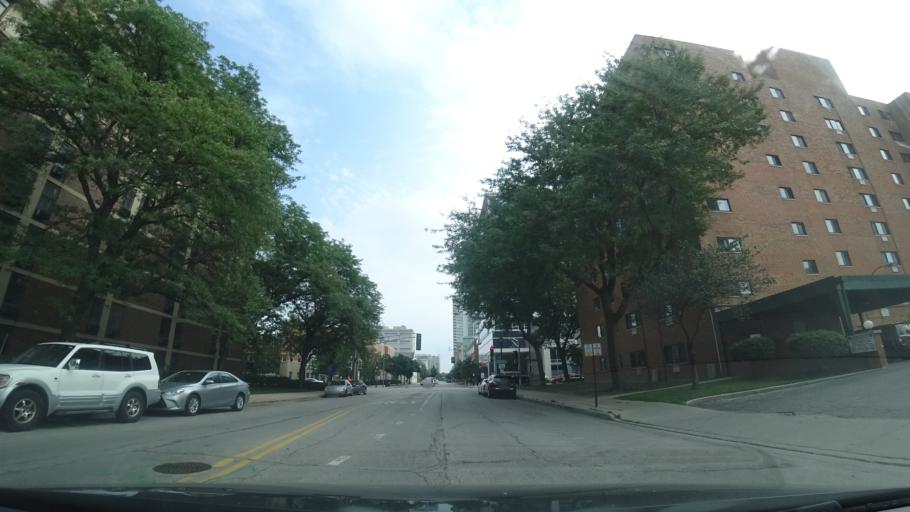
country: US
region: Illinois
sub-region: Cook County
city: Evanston
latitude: 42.0527
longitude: -87.6844
